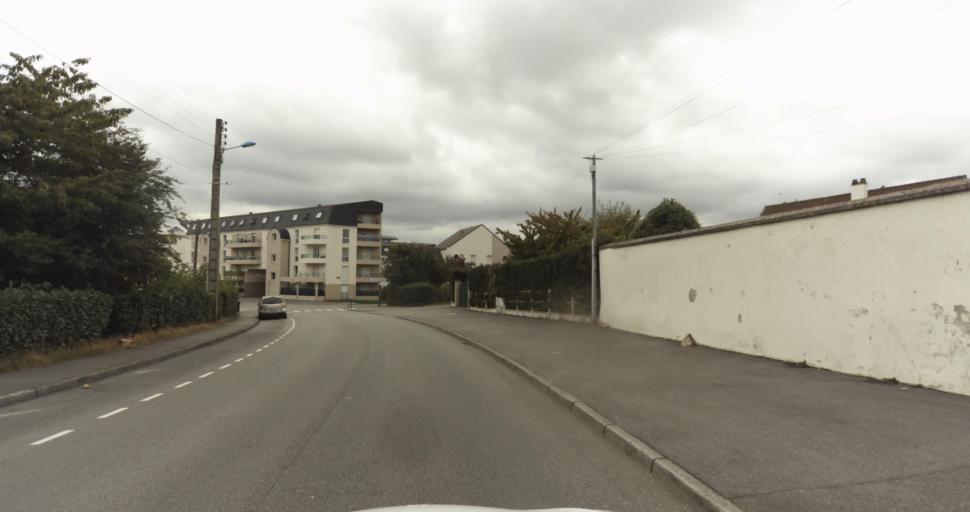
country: FR
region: Haute-Normandie
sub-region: Departement de l'Eure
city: Evreux
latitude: 49.0096
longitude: 1.1544
